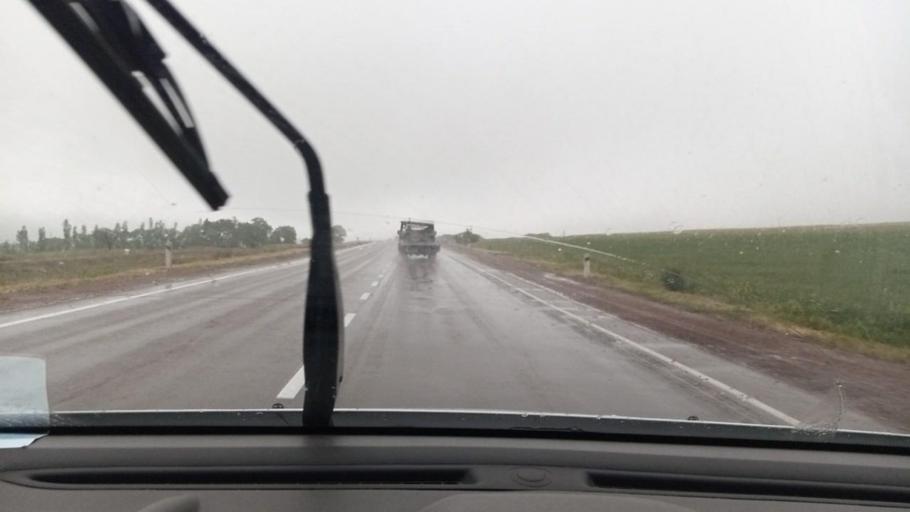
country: UZ
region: Toshkent
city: Angren
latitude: 41.0431
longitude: 70.1500
